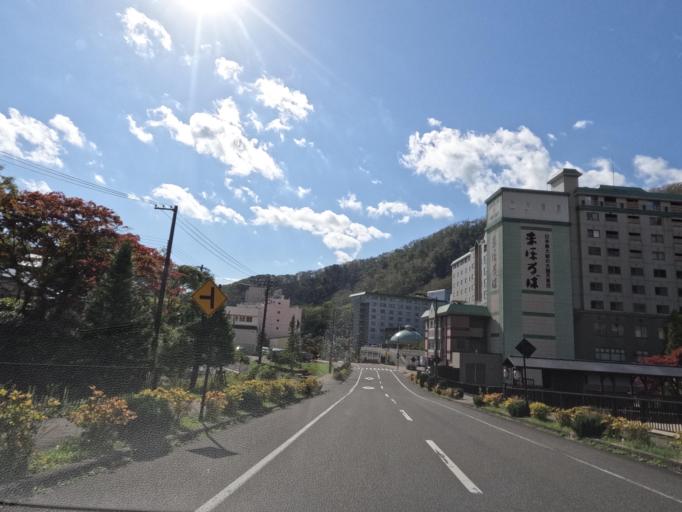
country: JP
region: Hokkaido
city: Shiraoi
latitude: 42.4943
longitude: 141.1426
